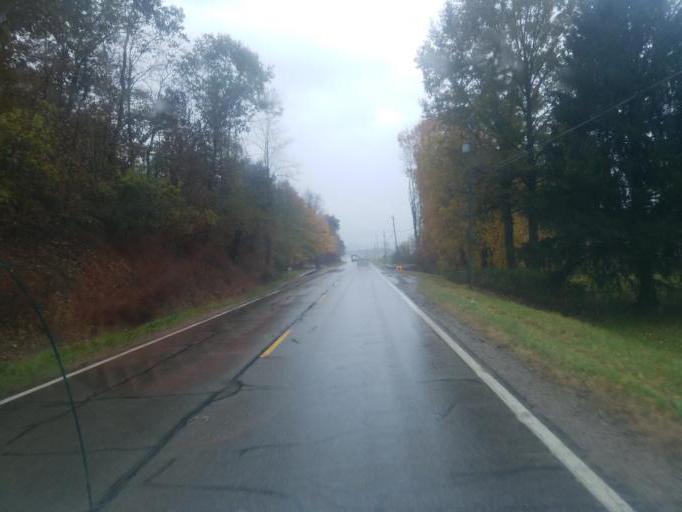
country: US
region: Ohio
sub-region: Muskingum County
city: South Zanesville
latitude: 39.8458
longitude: -81.8963
